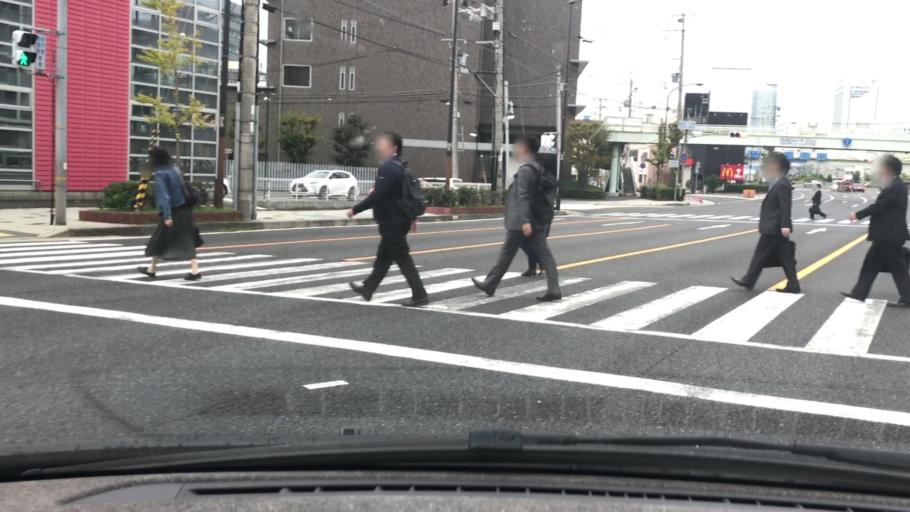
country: JP
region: Hyogo
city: Kobe
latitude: 34.7024
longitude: 135.2174
